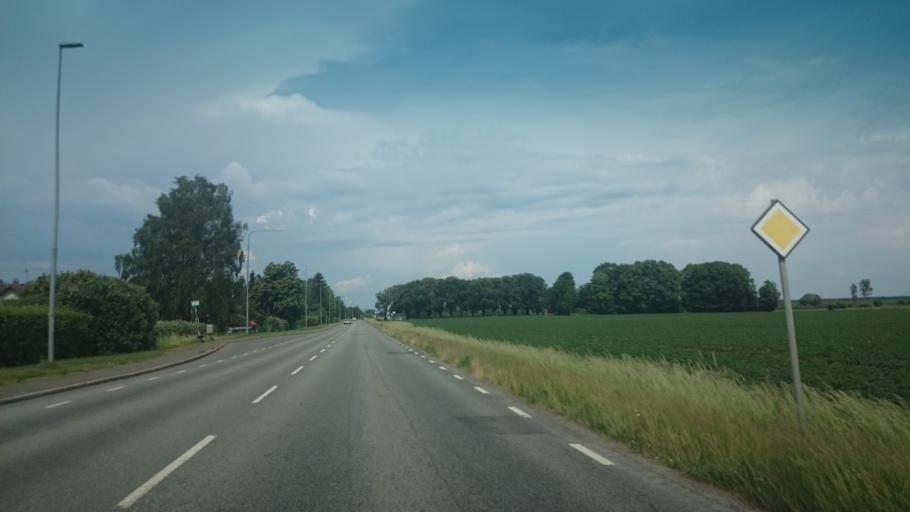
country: SE
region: Skane
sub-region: Kristianstads Kommun
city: Norra Asum
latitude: 55.9990
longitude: 14.1510
